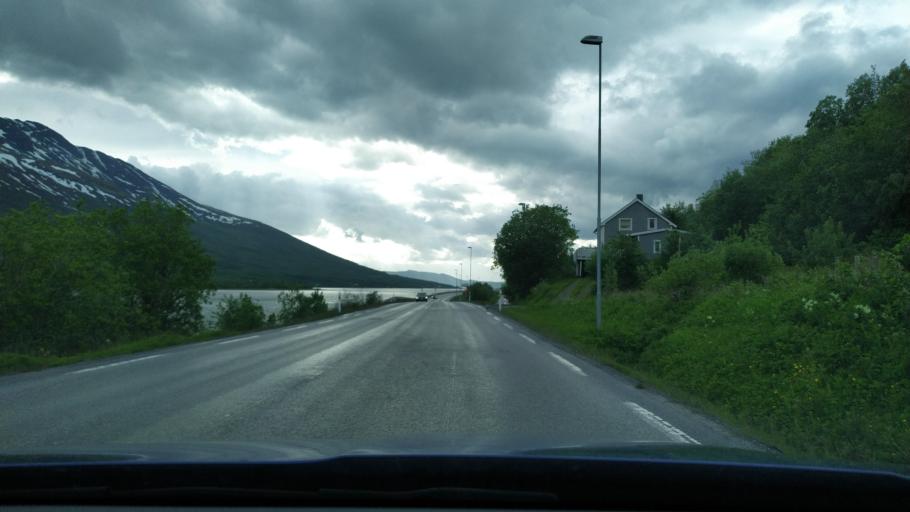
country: NO
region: Troms
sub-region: Balsfjord
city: Storsteinnes
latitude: 69.2218
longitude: 19.5227
